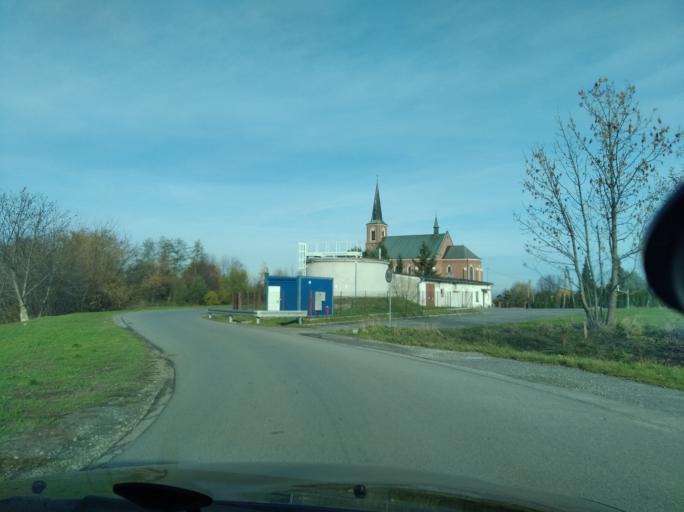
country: PL
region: Subcarpathian Voivodeship
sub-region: Powiat rzeszowski
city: Krasne
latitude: 50.0266
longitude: 22.1058
